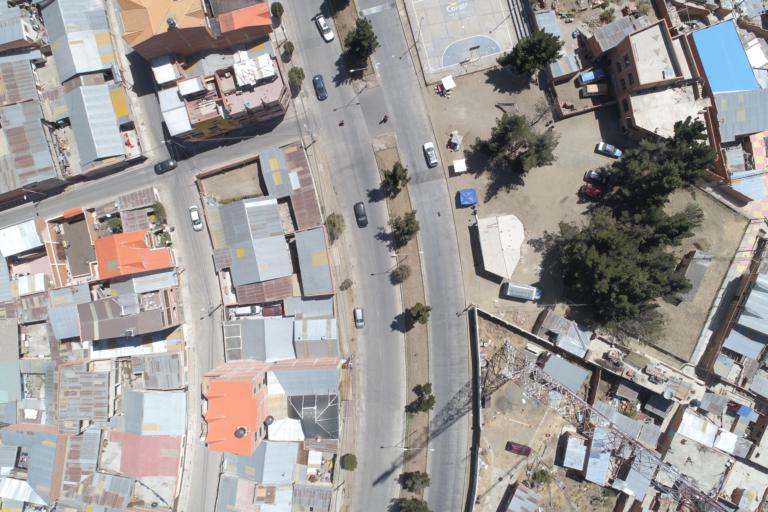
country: BO
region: La Paz
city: La Paz
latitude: -16.5217
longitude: -68.1487
